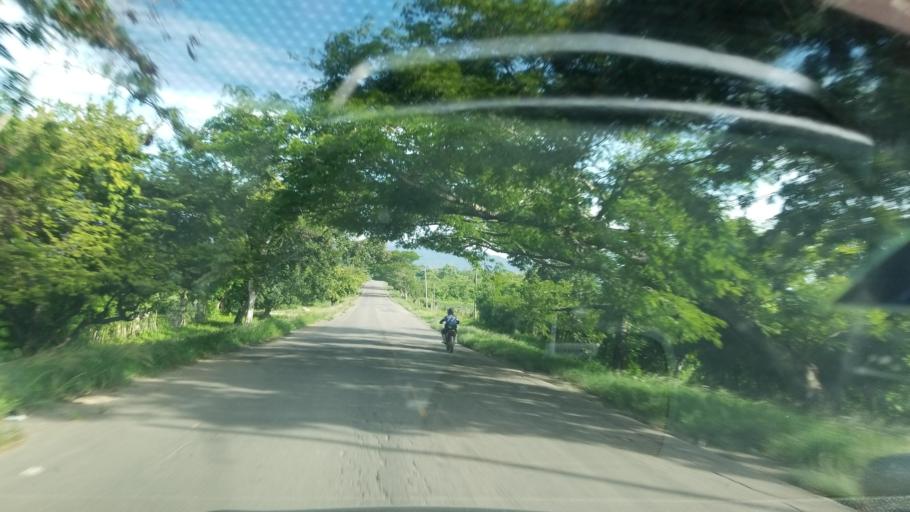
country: HN
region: El Paraiso
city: Cuyali
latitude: 13.9097
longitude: -86.5563
